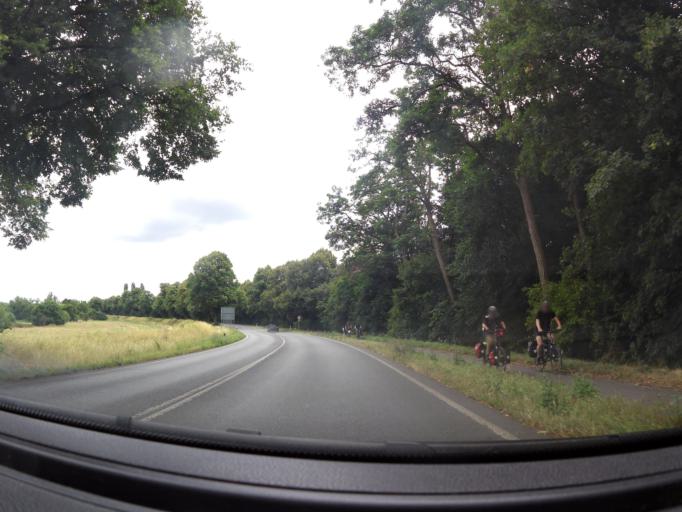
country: DE
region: North Rhine-Westphalia
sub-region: Regierungsbezirk Dusseldorf
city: Xanten
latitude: 51.6362
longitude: 6.4779
